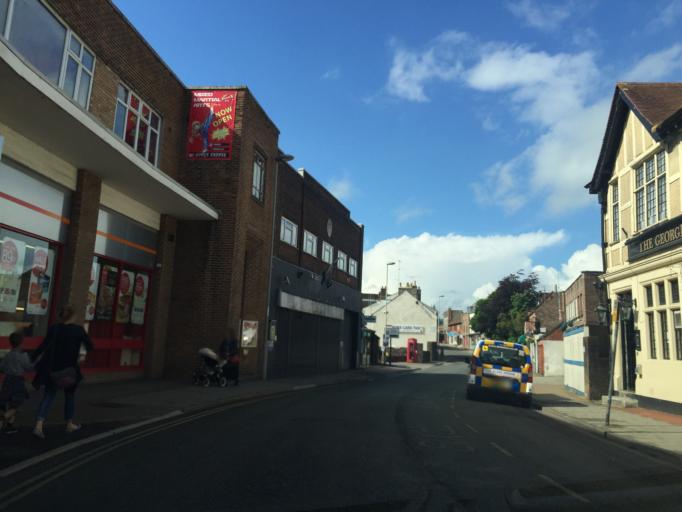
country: GB
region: England
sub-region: Dorset
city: Dorchester
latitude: 50.7122
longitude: -2.4380
